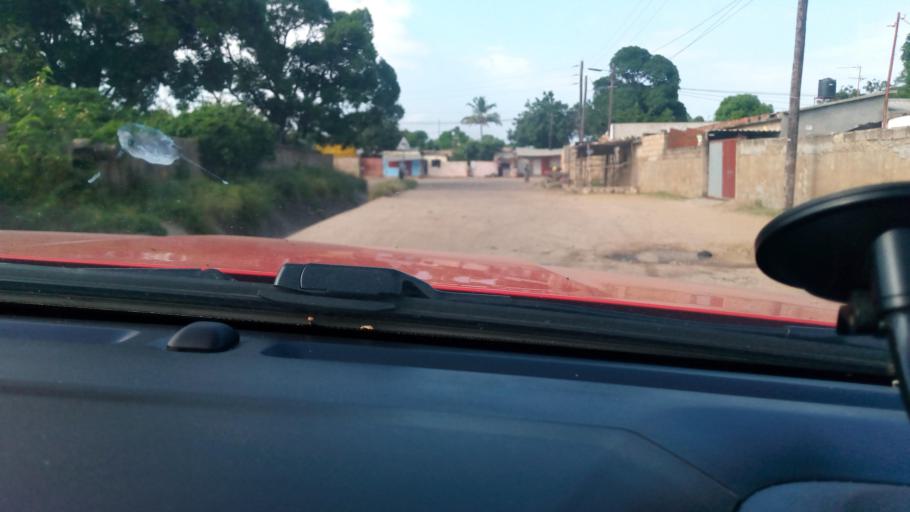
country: MZ
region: Maputo City
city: Maputo
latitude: -25.9325
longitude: 32.5464
